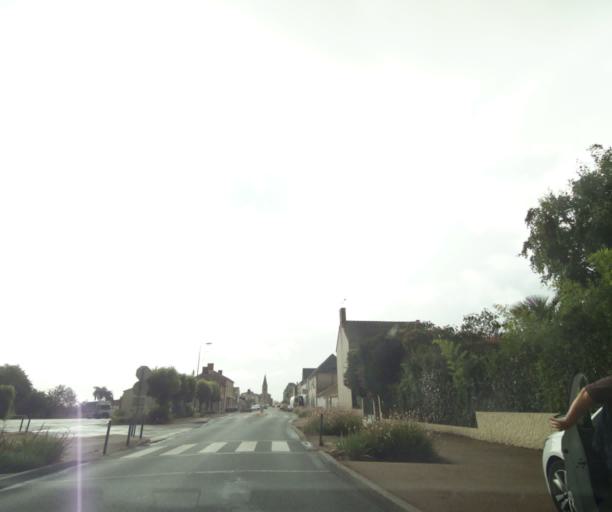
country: FR
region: Pays de la Loire
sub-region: Departement de la Vendee
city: Avrille
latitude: 46.4713
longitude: -1.4990
